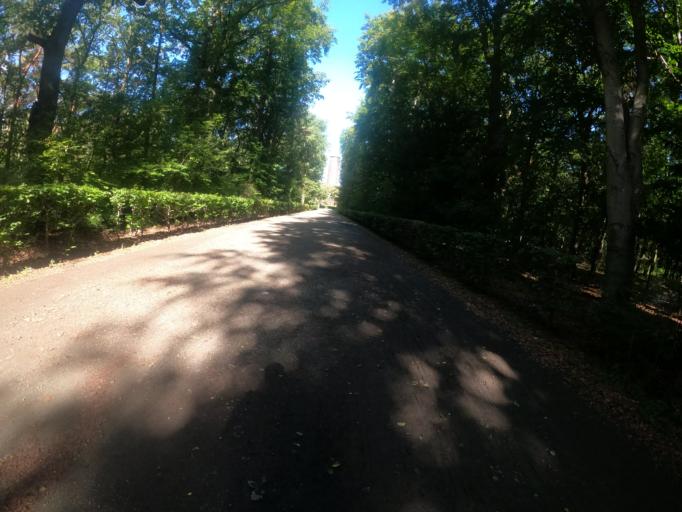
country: DE
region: Berlin
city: Charlottenburg-Nord
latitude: 52.5423
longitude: 13.2929
